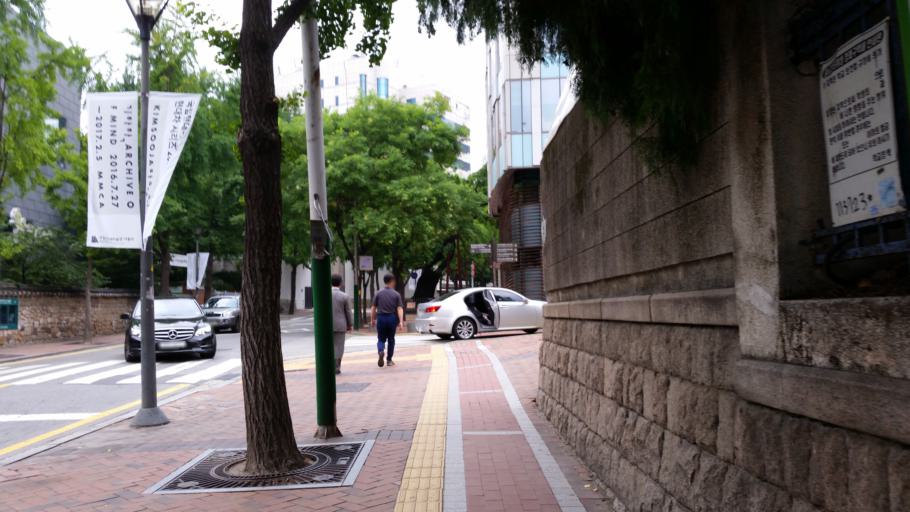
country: KR
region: Seoul
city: Seoul
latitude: 37.5665
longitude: 126.9712
